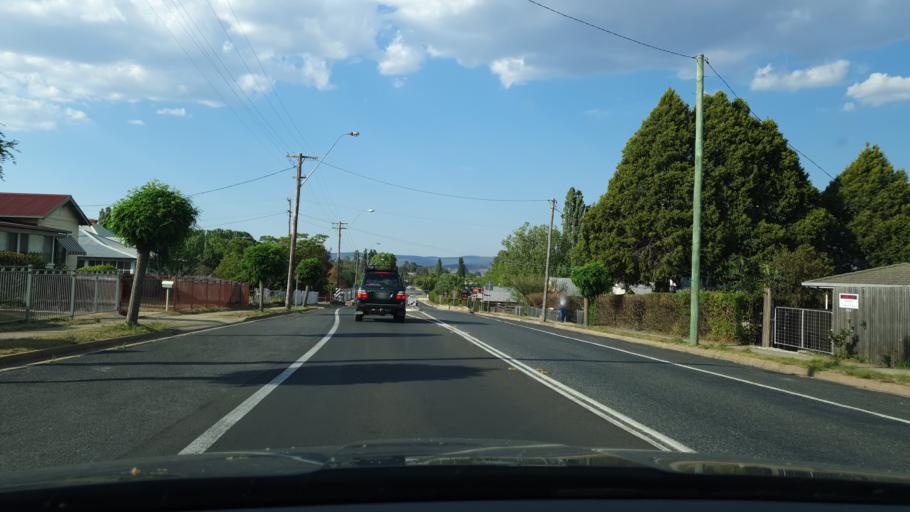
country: AU
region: New South Wales
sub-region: Tenterfield Municipality
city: Carrolls Creek
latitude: -29.0484
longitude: 152.0200
